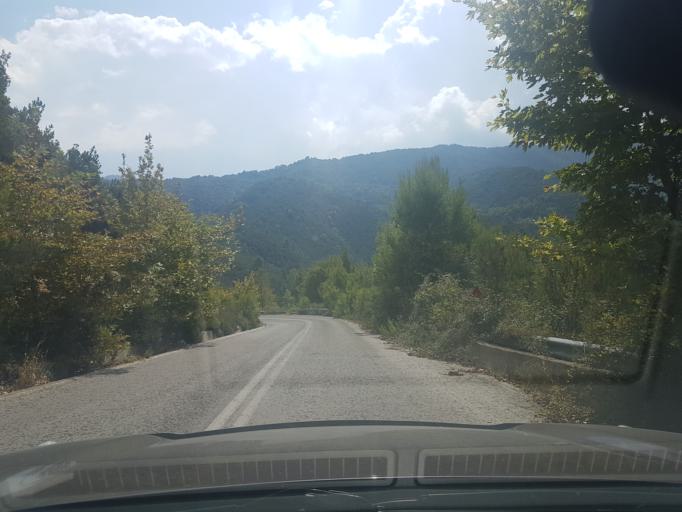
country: GR
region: Central Greece
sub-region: Nomos Evvoias
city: Kymi
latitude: 38.6527
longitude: 23.9213
